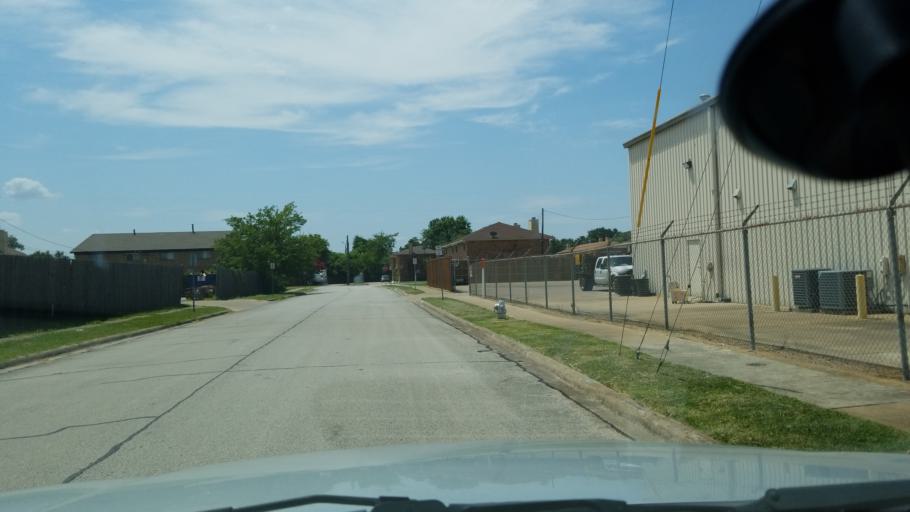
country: US
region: Texas
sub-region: Dallas County
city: Irving
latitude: 32.8149
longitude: -96.9868
